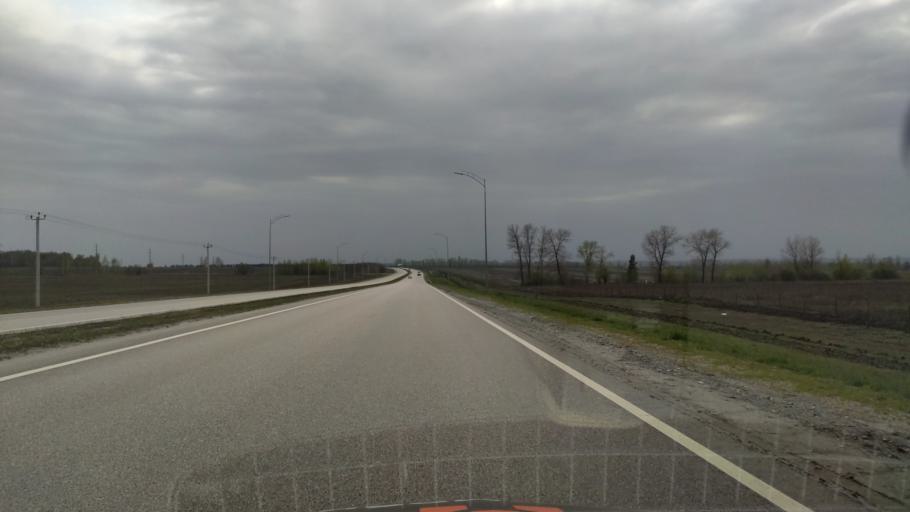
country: RU
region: Belgorod
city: Staryy Oskol
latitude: 51.3852
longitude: 37.8598
